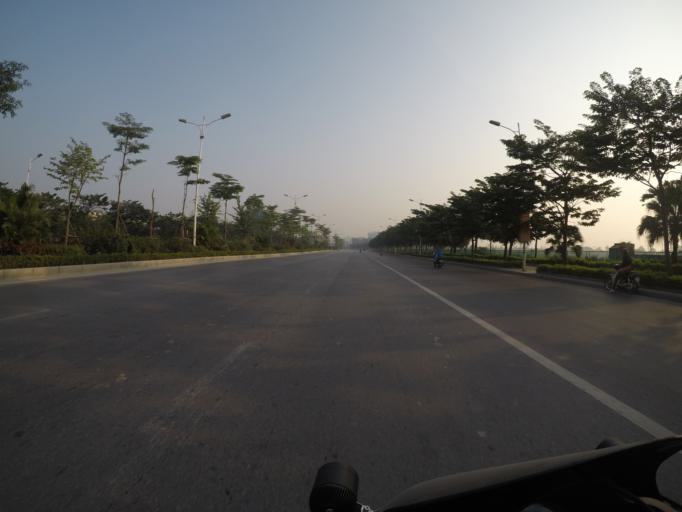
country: VN
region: Ha Noi
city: Trau Quy
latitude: 21.0299
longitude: 105.8989
